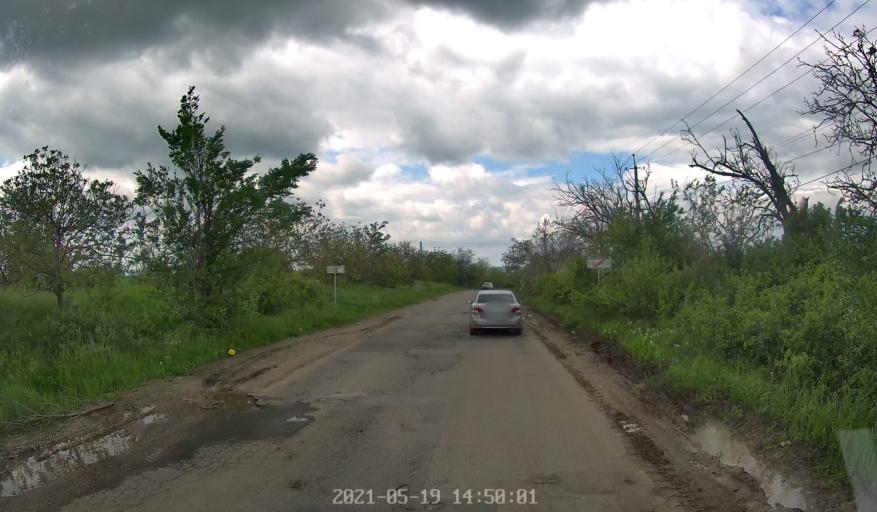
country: MD
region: Chisinau
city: Stauceni
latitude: 47.0536
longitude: 28.9478
